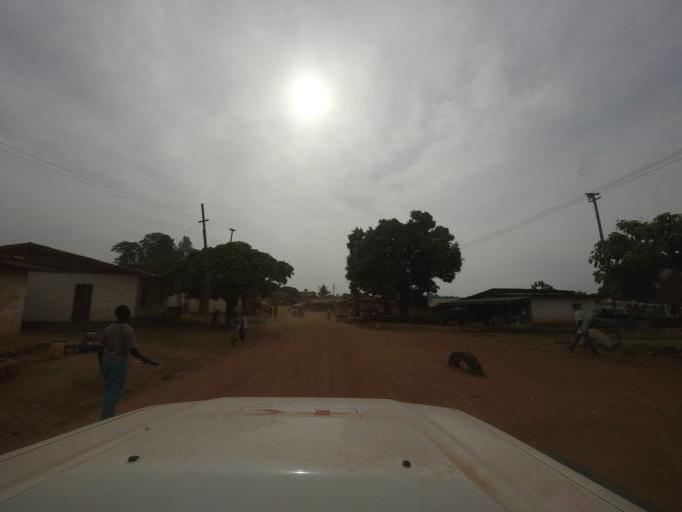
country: SL
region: Eastern Province
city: Buedu
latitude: 8.3597
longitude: -10.2099
